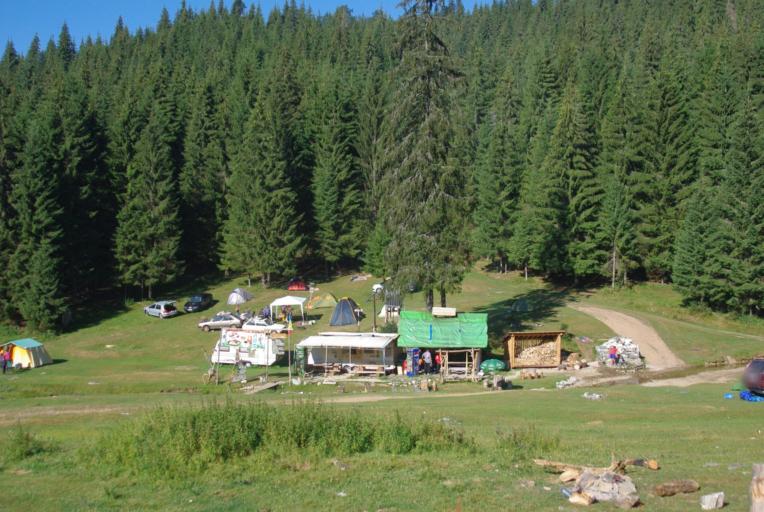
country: RO
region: Alba
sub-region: Comuna Arieseni
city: Arieseni
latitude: 46.5790
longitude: 22.7036
